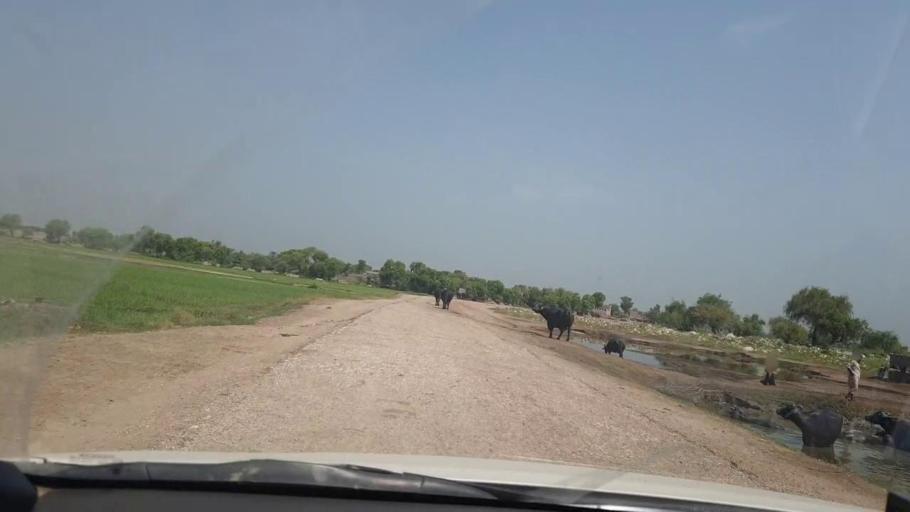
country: PK
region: Sindh
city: Chak
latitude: 27.8783
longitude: 68.7826
